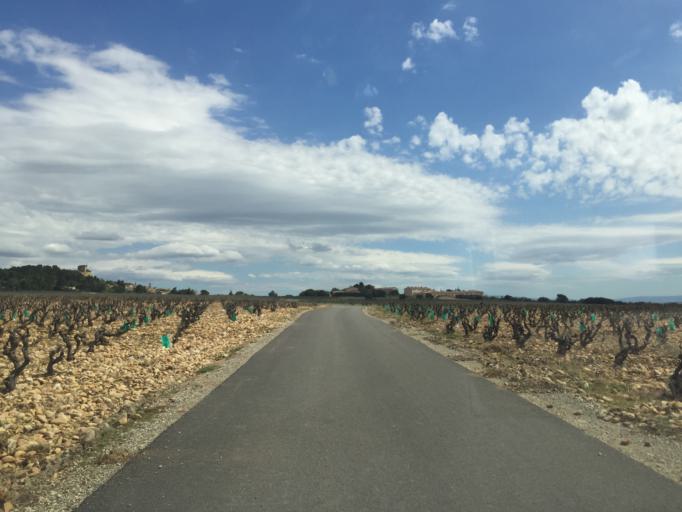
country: FR
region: Provence-Alpes-Cote d'Azur
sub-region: Departement du Vaucluse
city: Chateauneuf-du-Pape
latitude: 44.0553
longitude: 4.8151
